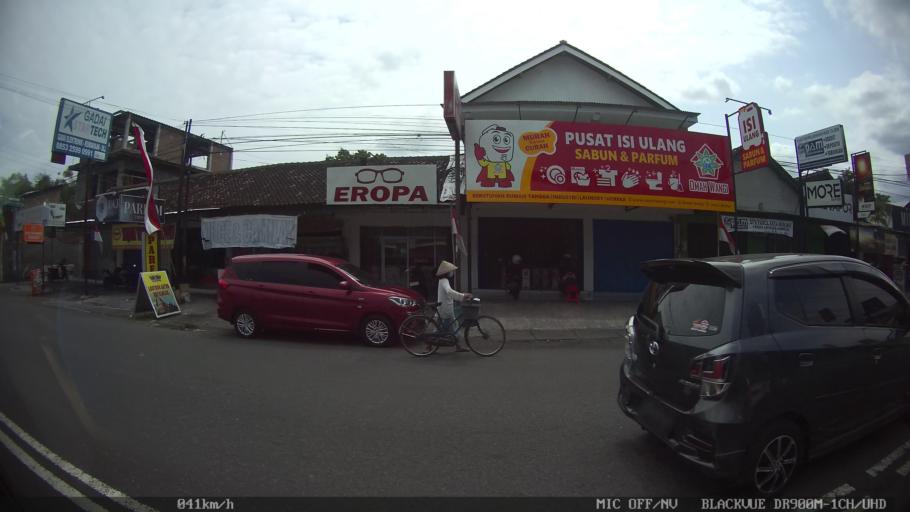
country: ID
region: Daerah Istimewa Yogyakarta
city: Depok
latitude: -7.7575
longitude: 110.4336
